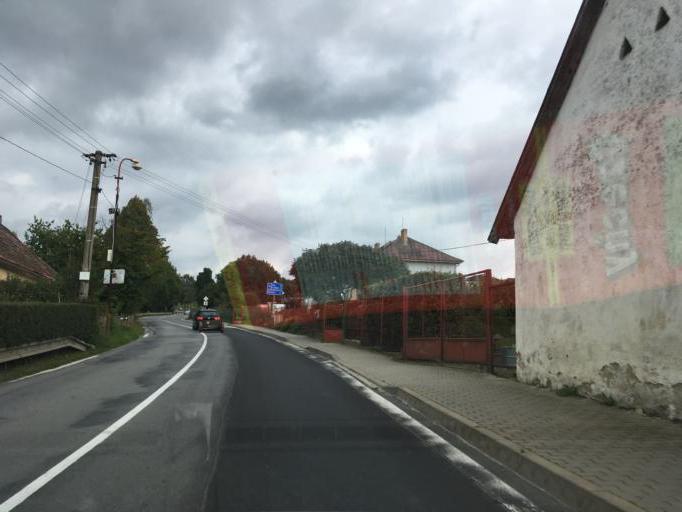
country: CZ
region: Vysocina
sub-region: Okres Pelhrimov
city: Pelhrimov
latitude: 49.3885
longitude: 15.2355
